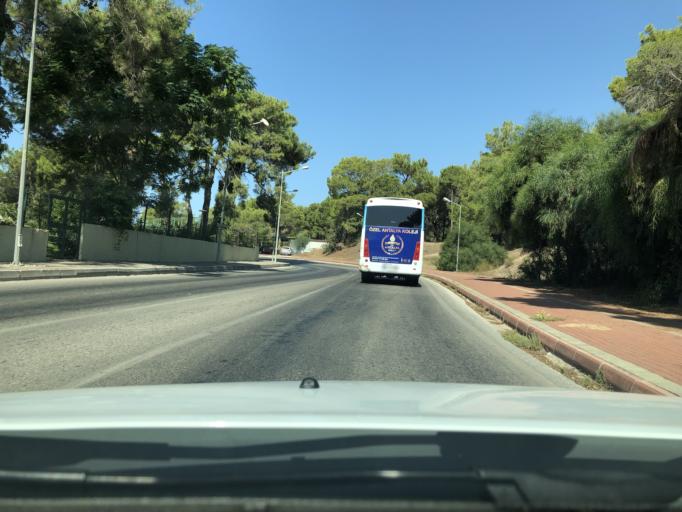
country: TR
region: Antalya
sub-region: Manavgat
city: Manavgat
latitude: 36.7587
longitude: 31.4281
